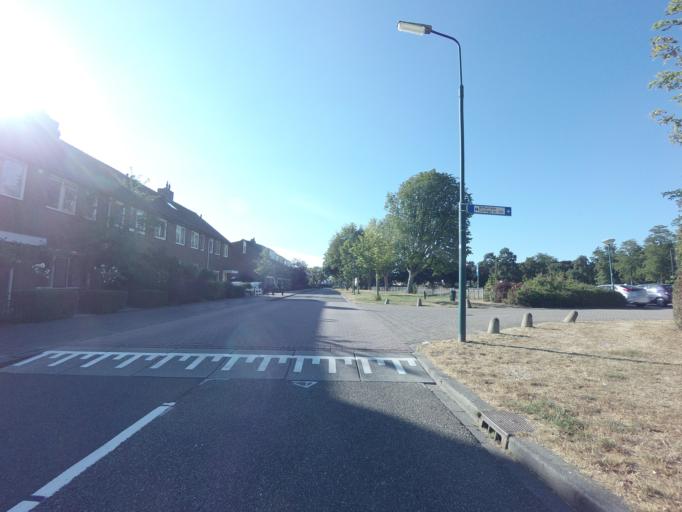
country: NL
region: Utrecht
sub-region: Stichtse Vecht
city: Spechtenkamp
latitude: 52.1351
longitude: 5.0218
